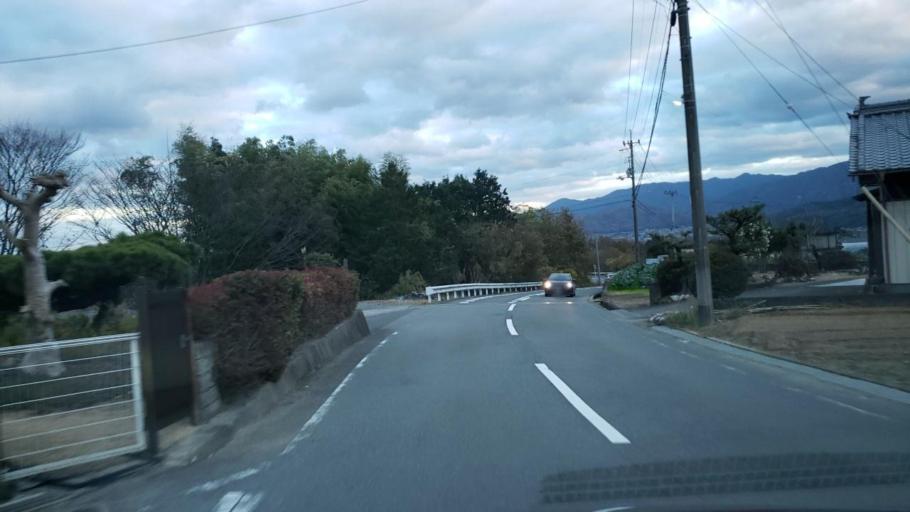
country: JP
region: Tokushima
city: Wakimachi
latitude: 34.0840
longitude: 134.1876
